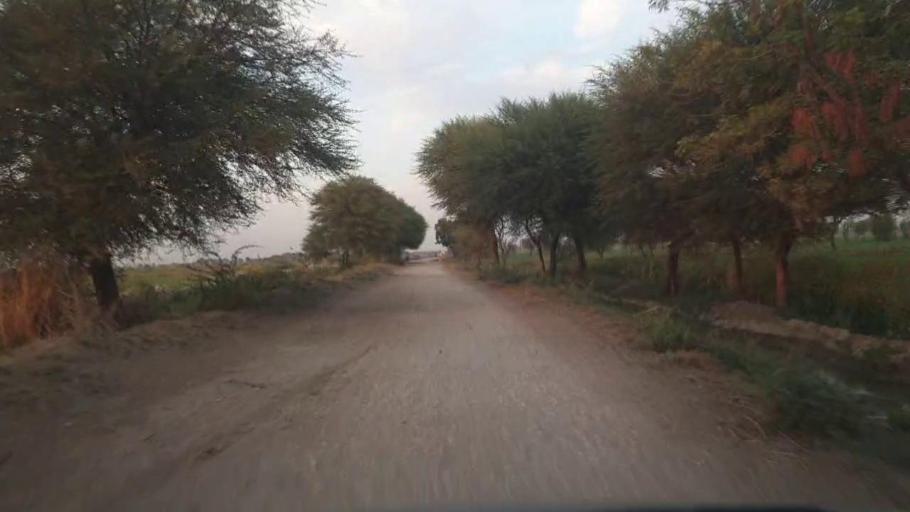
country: PK
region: Sindh
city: Umarkot
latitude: 25.2718
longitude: 69.6797
